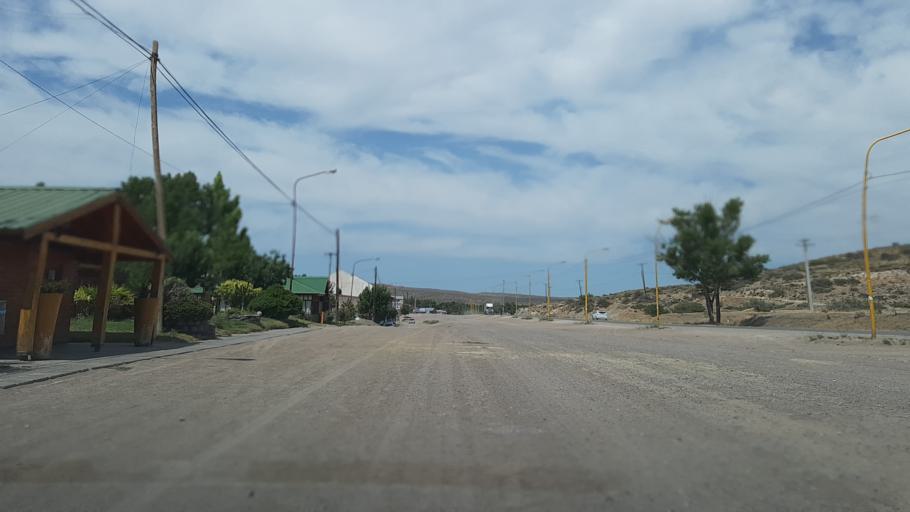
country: AR
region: Neuquen
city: Piedra del Aguila
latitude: -40.0440
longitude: -70.0717
